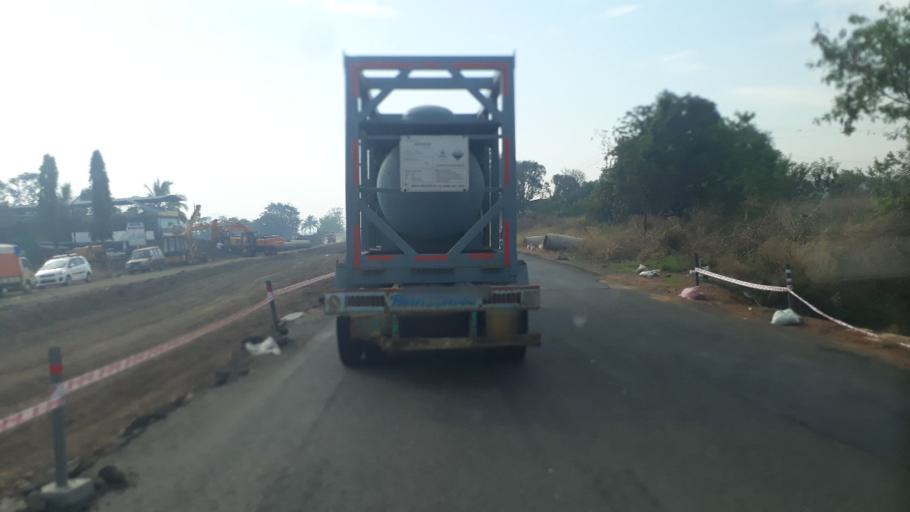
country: IN
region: Maharashtra
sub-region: Raigarh
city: Pen
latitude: 18.8050
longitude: 73.0909
